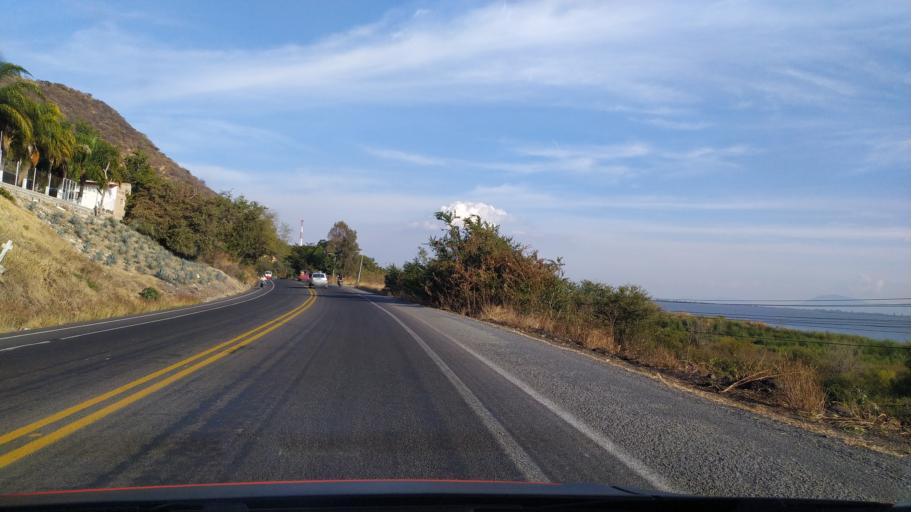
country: MX
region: Jalisco
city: Jamay
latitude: 20.2940
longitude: -102.7514
